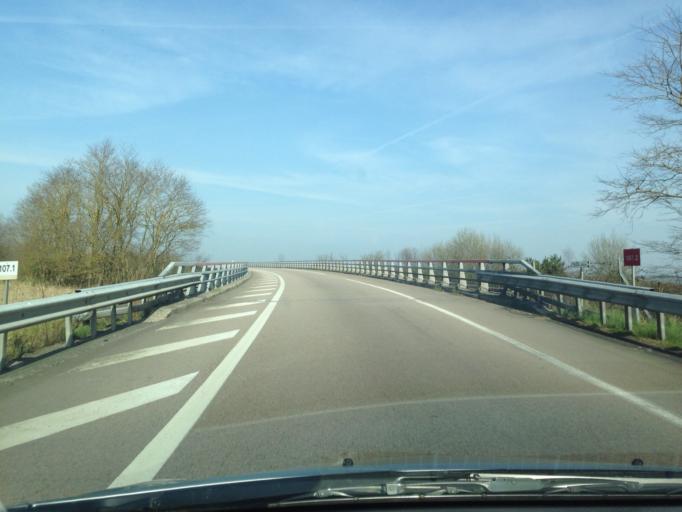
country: FR
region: Haute-Normandie
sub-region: Departement de la Seine-Maritime
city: Saint-Saens
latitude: 49.6497
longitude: 1.2655
